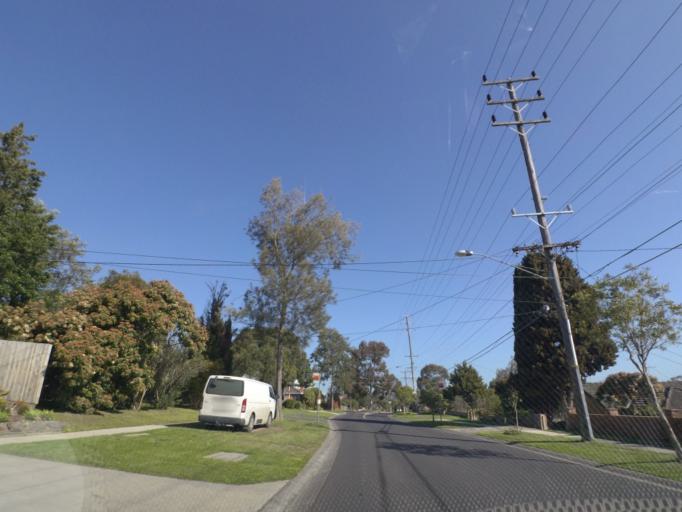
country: AU
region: Victoria
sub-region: Boroondara
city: Balwyn North
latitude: -37.7784
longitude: 145.1038
